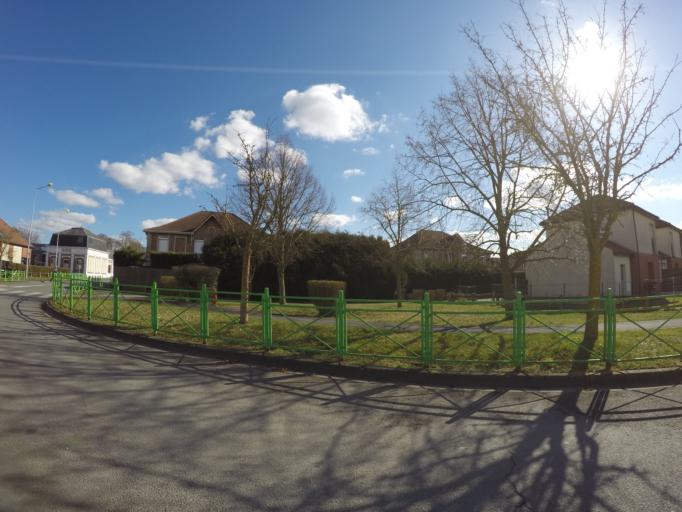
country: FR
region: Nord-Pas-de-Calais
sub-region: Departement du Pas-de-Calais
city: Mazingarbe
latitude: 50.4579
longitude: 2.7213
